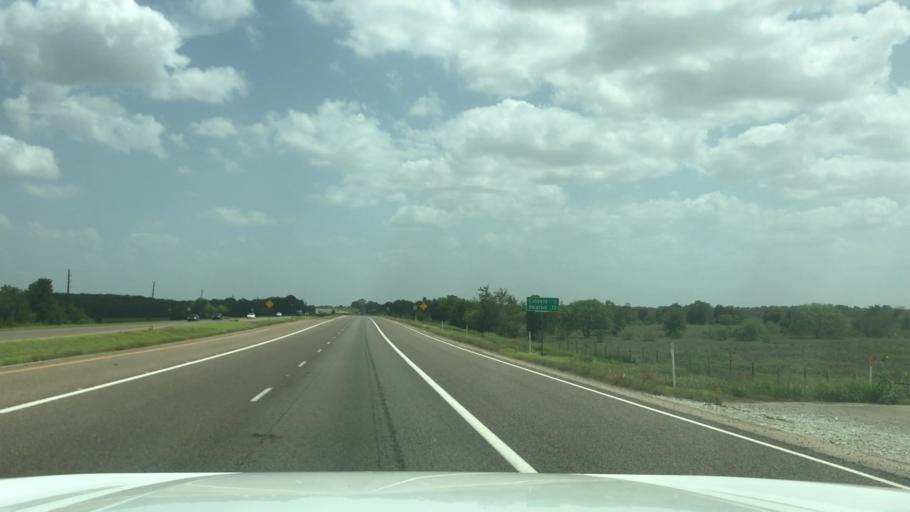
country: US
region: Texas
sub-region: Robertson County
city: Calvert
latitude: 31.0191
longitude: -96.7068
